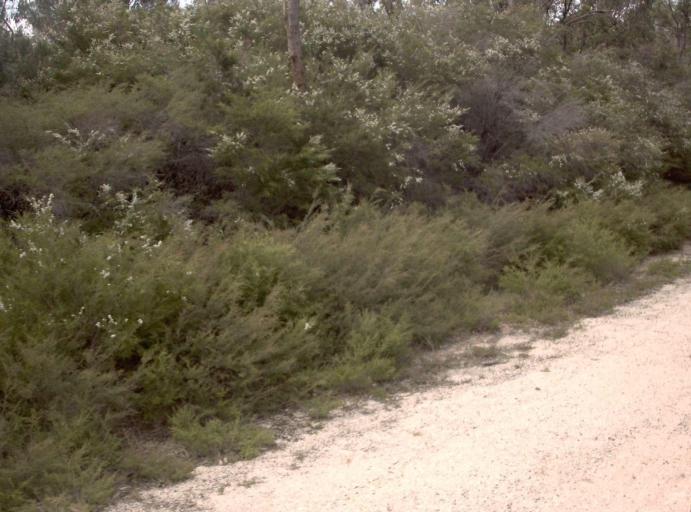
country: AU
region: New South Wales
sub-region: Bega Valley
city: Eden
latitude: -37.4198
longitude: 149.6501
